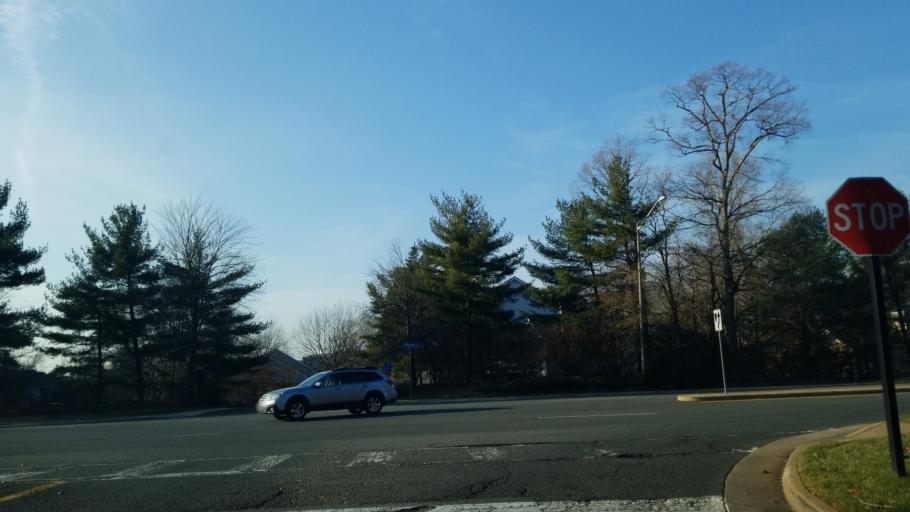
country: US
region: Virginia
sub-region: Fairfax County
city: Greenbriar
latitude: 38.8569
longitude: -77.3969
